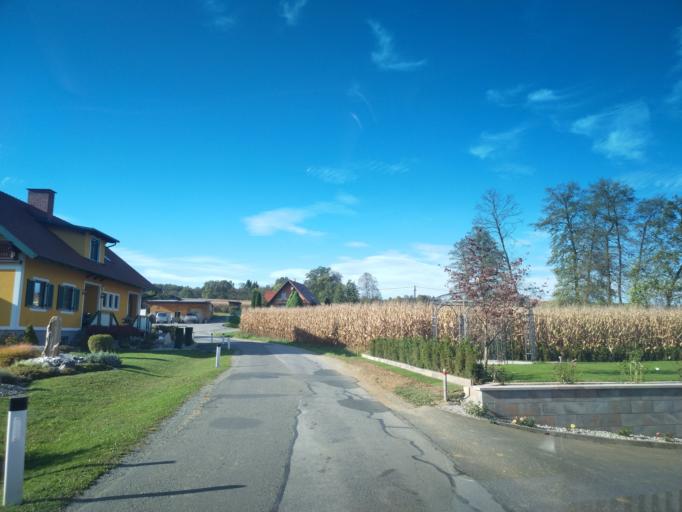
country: AT
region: Styria
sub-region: Politischer Bezirk Leibnitz
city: Sankt Johann im Saggautal
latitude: 46.7009
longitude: 15.3874
